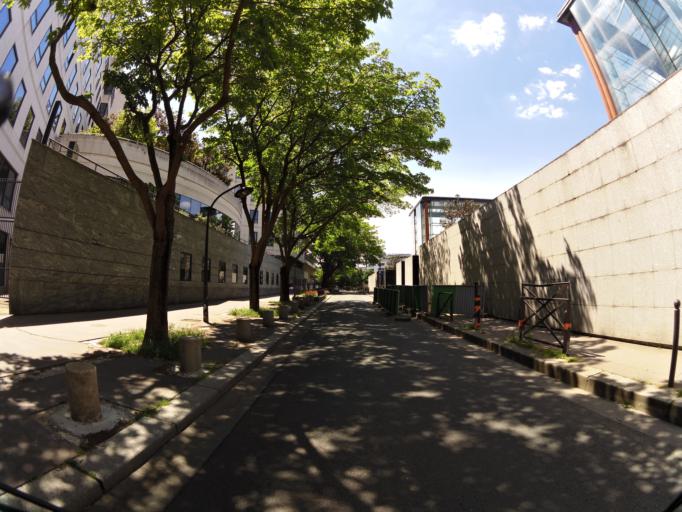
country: FR
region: Ile-de-France
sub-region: Departement des Hauts-de-Seine
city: Issy-les-Moulineaux
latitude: 48.8404
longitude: 2.2776
